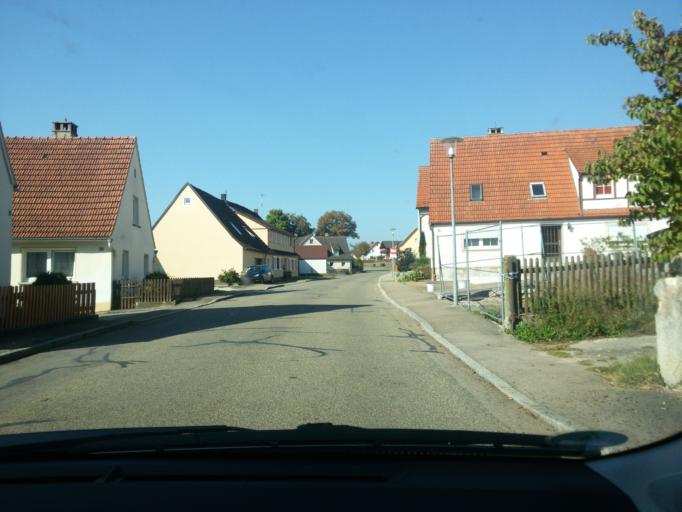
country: DE
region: Bavaria
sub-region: Regierungsbezirk Mittelfranken
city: Wassertrudingen
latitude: 49.0027
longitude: 10.5824
